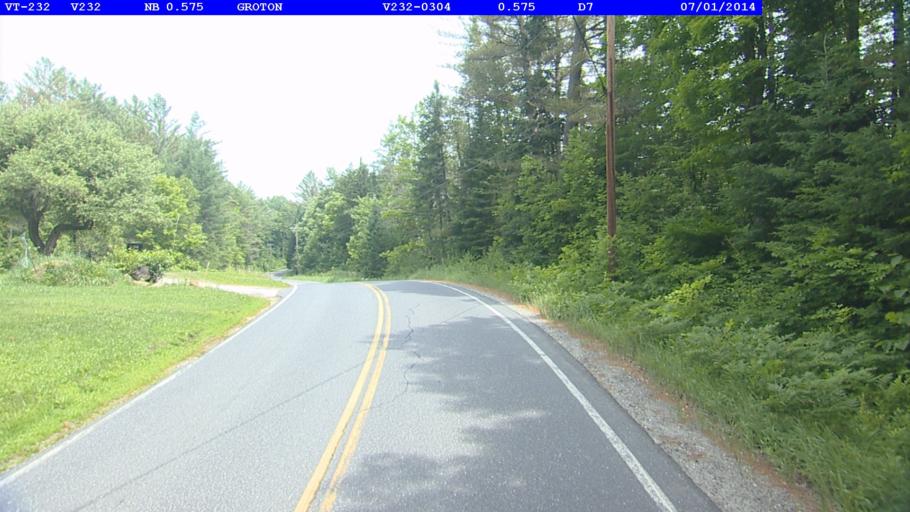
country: US
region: New Hampshire
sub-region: Grafton County
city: Woodsville
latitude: 44.2273
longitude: -72.2288
